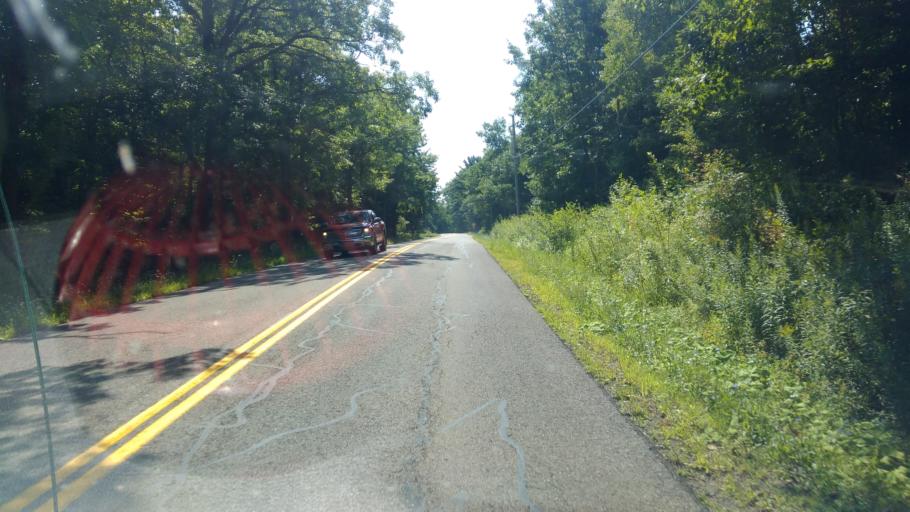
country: US
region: New York
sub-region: Allegany County
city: Belmont
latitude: 42.2872
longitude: -77.9954
